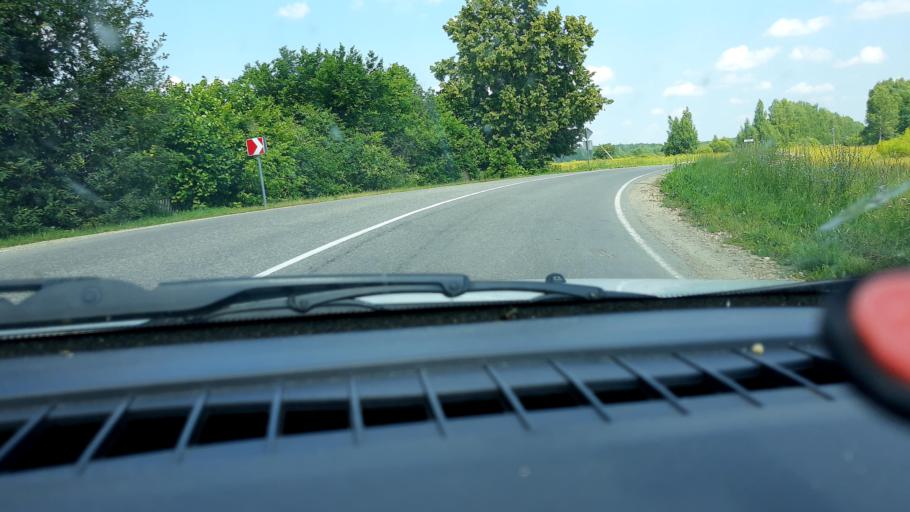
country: RU
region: Nizjnij Novgorod
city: Sharanga
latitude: 57.1292
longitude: 46.5095
